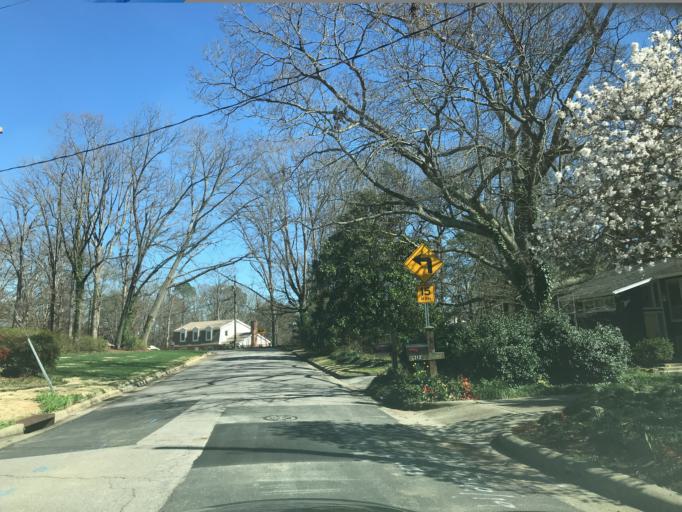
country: US
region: North Carolina
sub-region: Wake County
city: West Raleigh
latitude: 35.8517
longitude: -78.6382
